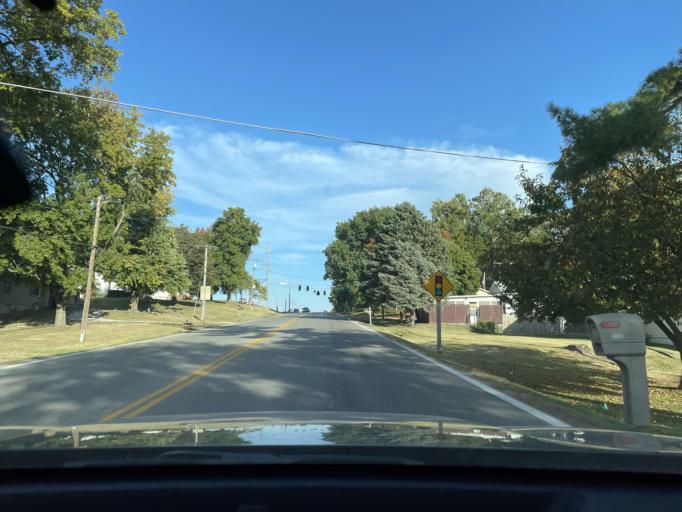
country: US
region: Missouri
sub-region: Buchanan County
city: Saint Joseph
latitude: 39.7552
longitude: -94.7983
